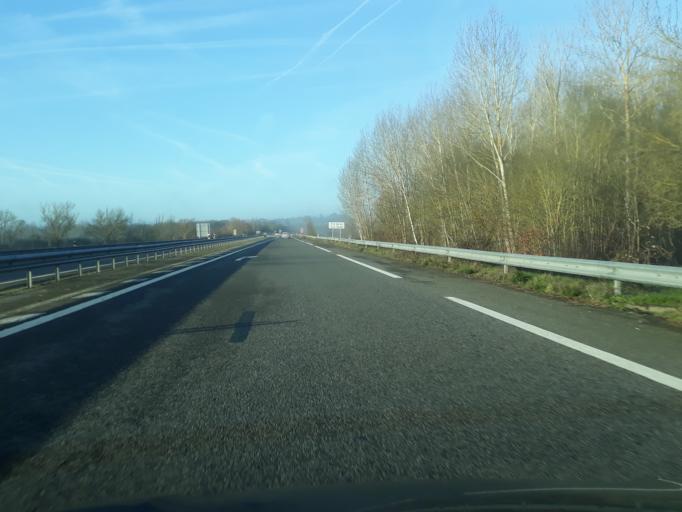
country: FR
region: Midi-Pyrenees
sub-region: Departement du Gers
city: Pujaudran
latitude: 43.6063
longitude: 1.0610
